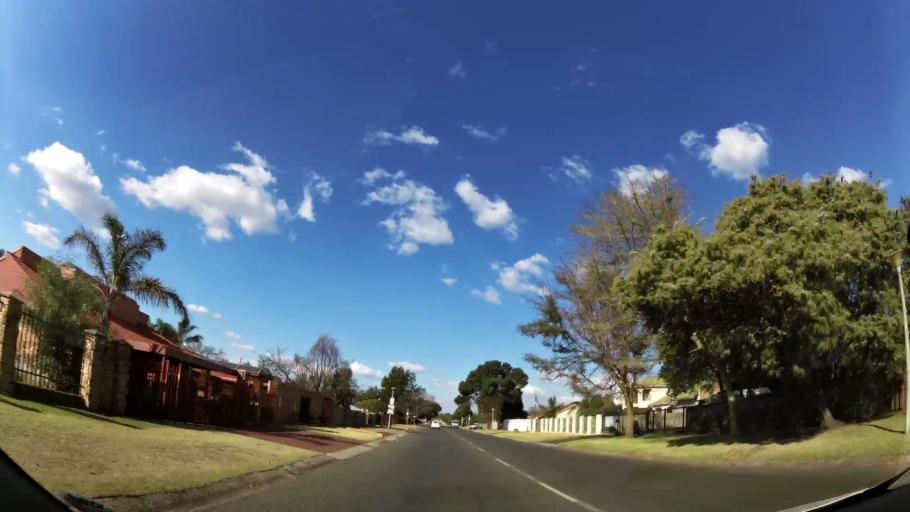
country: ZA
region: Mpumalanga
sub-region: Nkangala District Municipality
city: Witbank
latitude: -25.8957
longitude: 29.2401
